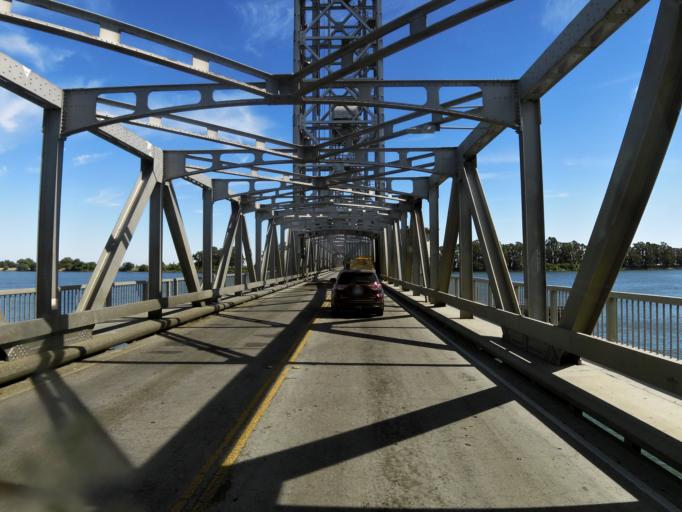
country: US
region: California
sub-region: Solano County
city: Rio Vista
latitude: 38.1596
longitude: -121.6853
